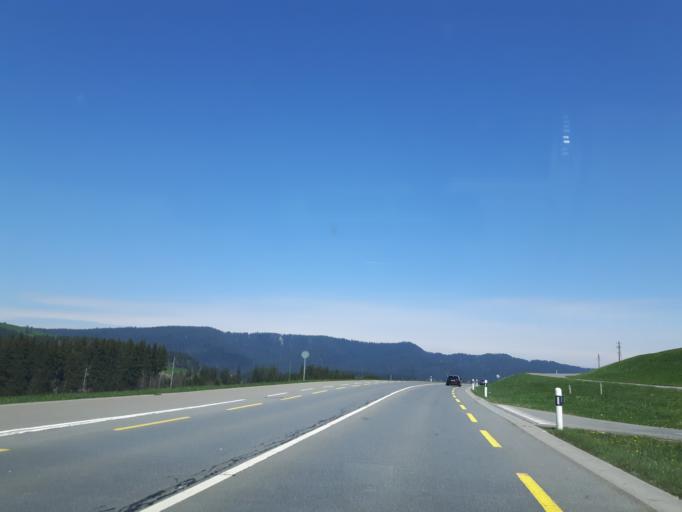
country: CH
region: Schwyz
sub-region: Bezirk Schwyz
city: Rothenthurm
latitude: 47.1224
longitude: 8.6891
